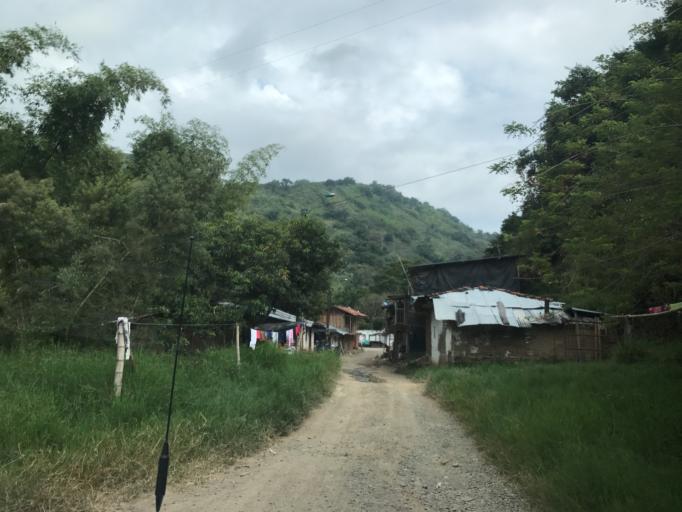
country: CO
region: Valle del Cauca
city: Obando
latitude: 4.5520
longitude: -75.8757
